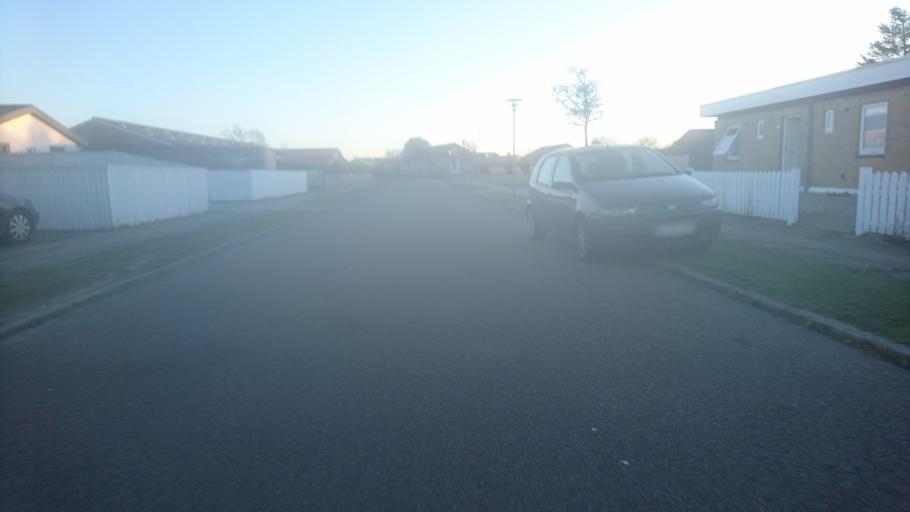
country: DK
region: North Denmark
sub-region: Frederikshavn Kommune
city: Skagen
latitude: 57.7265
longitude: 10.5764
